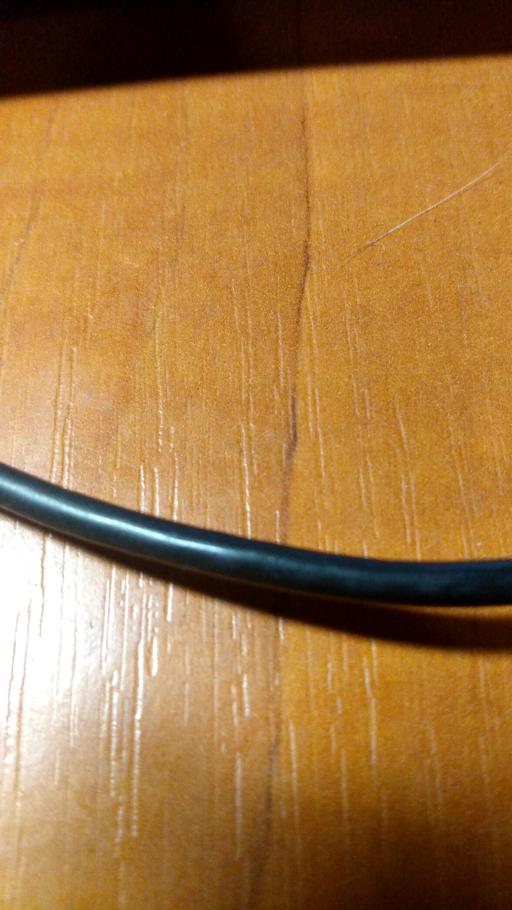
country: RU
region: Tverskaya
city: Toropets
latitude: 56.5069
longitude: 31.1408
